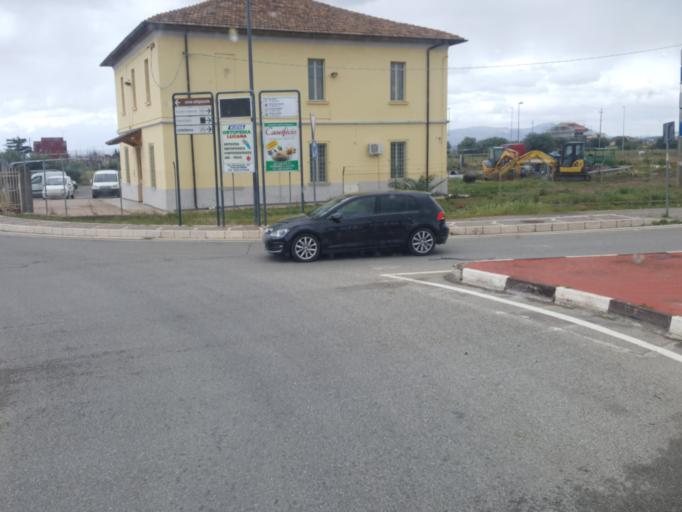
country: IT
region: Basilicate
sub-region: Provincia di Matera
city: Scanzano Jonico
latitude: 40.2487
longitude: 16.6980
